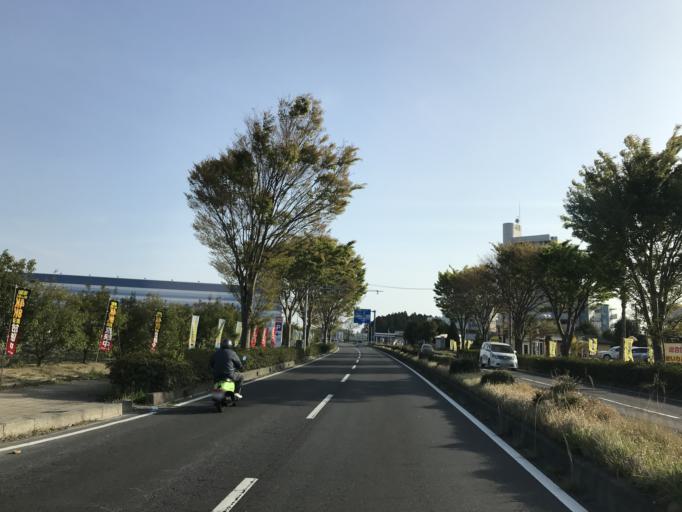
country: JP
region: Ibaraki
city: Hitachi-Naka
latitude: 36.4065
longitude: 140.5818
